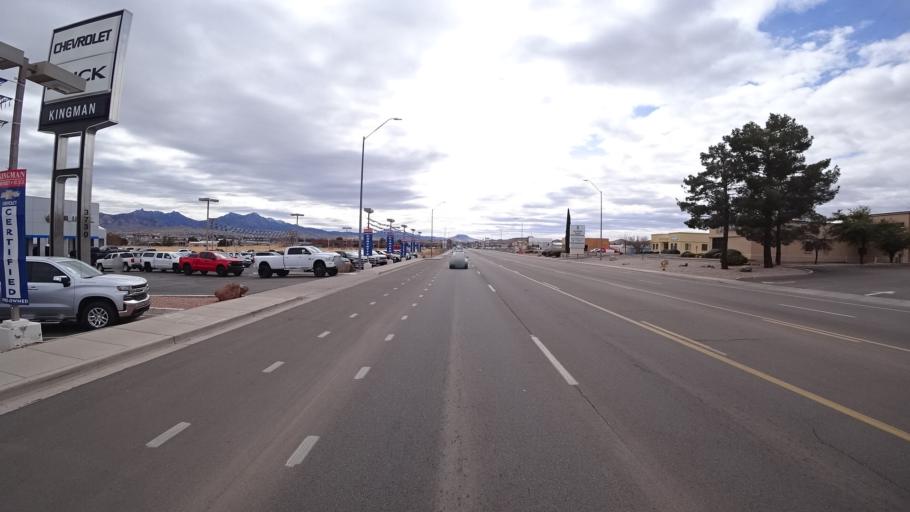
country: US
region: Arizona
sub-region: Mohave County
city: New Kingman-Butler
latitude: 35.2317
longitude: -114.0369
